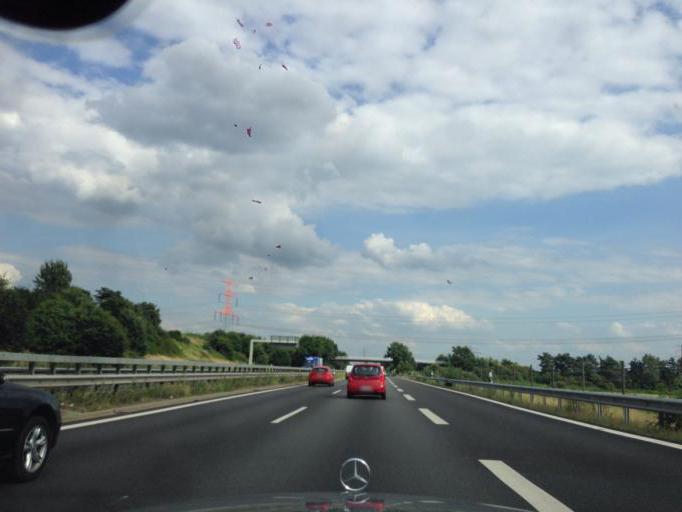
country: DE
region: Schleswig-Holstein
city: Oststeinbek
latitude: 53.4798
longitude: 10.1530
